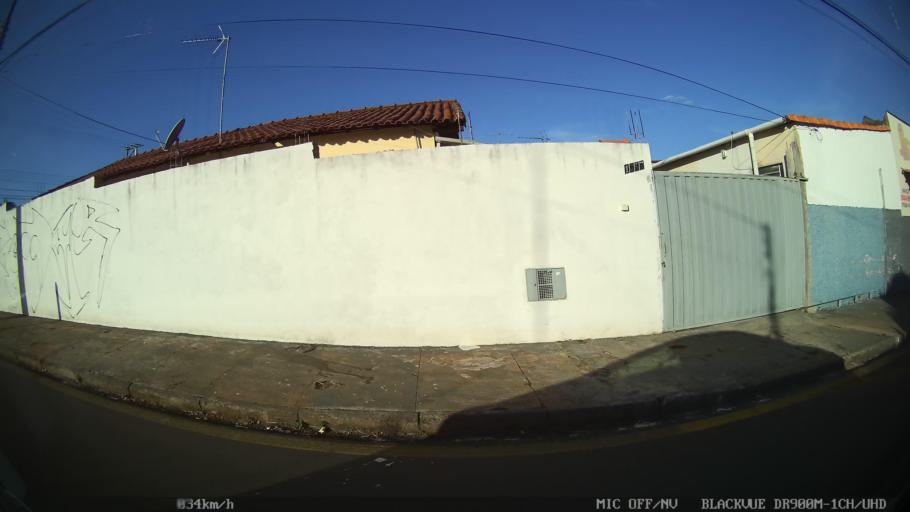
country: BR
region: Sao Paulo
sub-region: Franca
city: Franca
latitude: -20.5288
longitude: -47.3776
